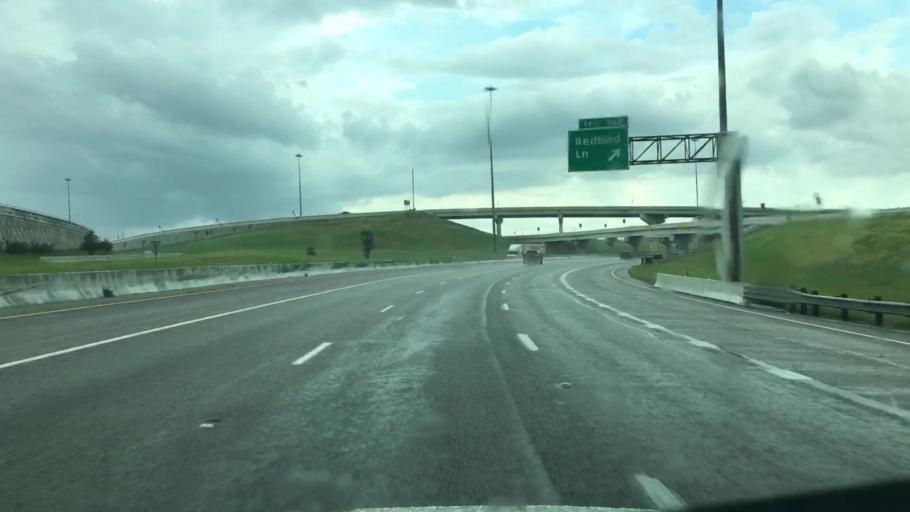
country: US
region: Texas
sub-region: Nueces County
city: Robstown
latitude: 27.8624
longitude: -97.6196
